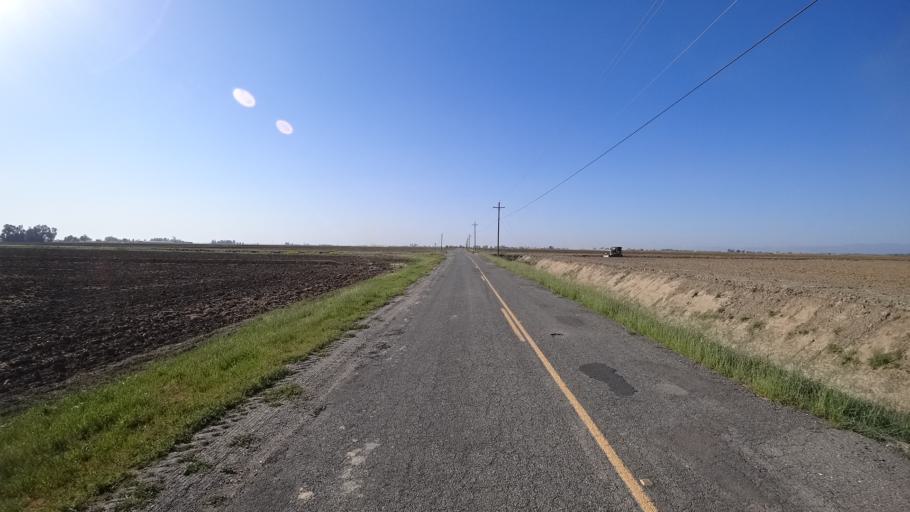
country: US
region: California
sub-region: Glenn County
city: Willows
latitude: 39.5615
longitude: -122.1171
